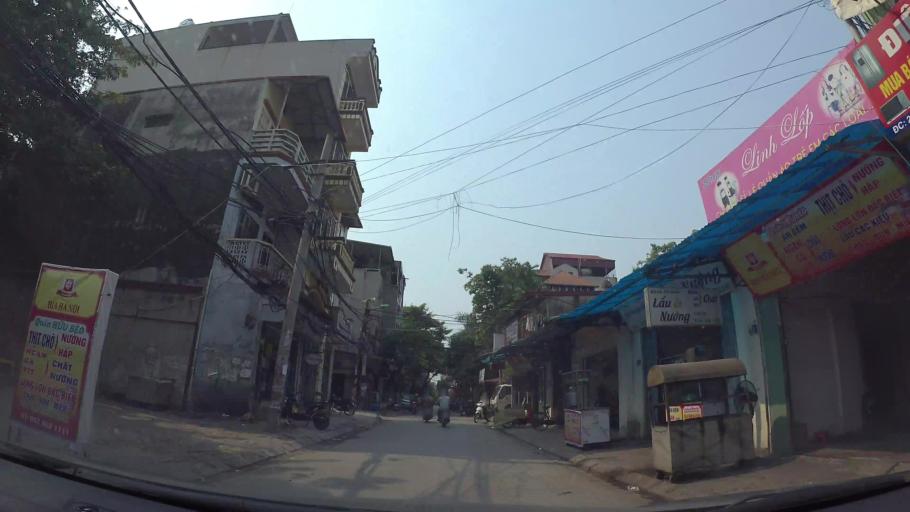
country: VN
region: Ha Noi
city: Thanh Xuan
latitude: 20.9870
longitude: 105.8188
